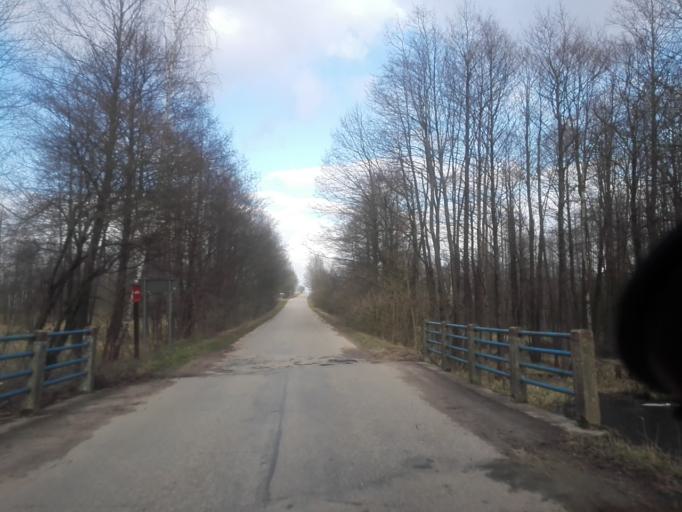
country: PL
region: Podlasie
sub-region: Suwalki
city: Suwalki
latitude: 54.2195
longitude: 22.8150
